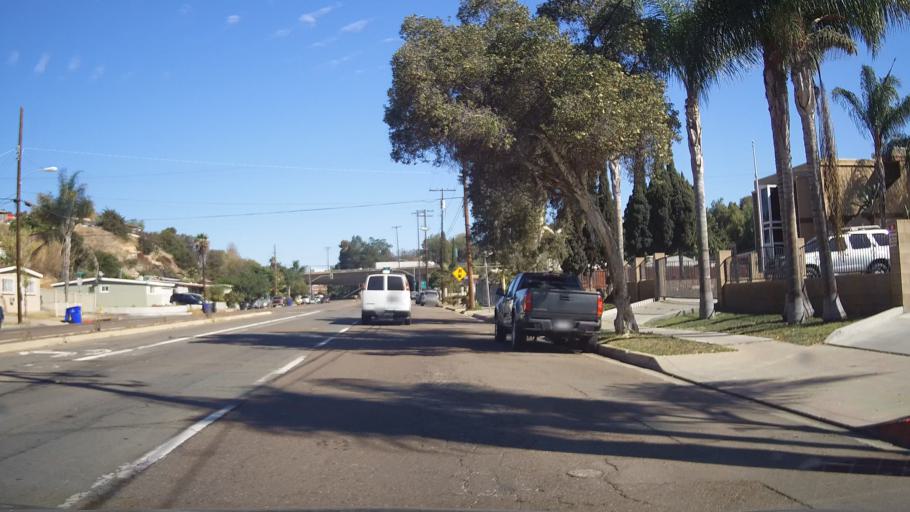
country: US
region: California
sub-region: San Diego County
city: National City
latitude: 32.7242
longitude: -117.1058
